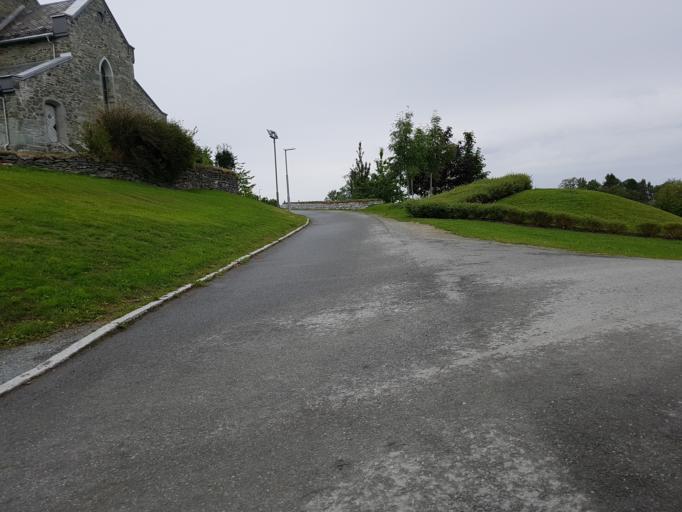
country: NO
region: Sor-Trondelag
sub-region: Trondheim
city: Trondheim
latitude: 63.4045
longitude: 10.3714
